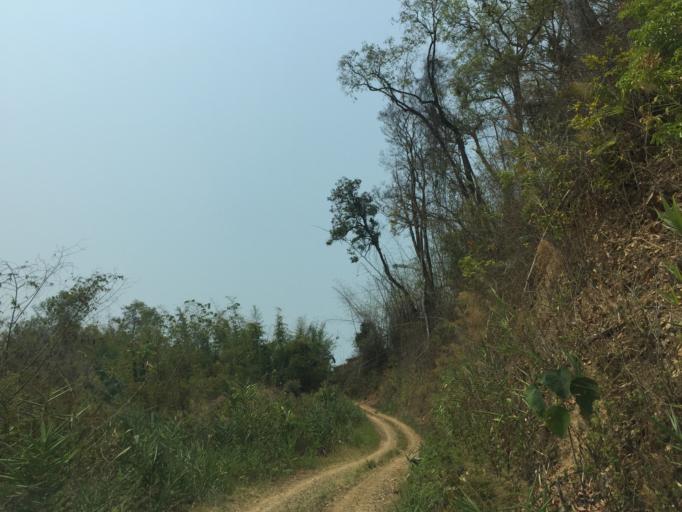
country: LA
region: Loungnamtha
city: Muang Nale
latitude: 20.6187
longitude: 101.6086
